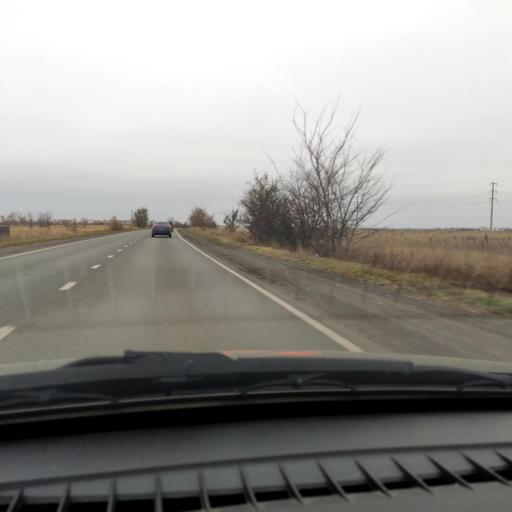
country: RU
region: Samara
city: Podstepki
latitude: 53.5185
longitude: 49.2090
